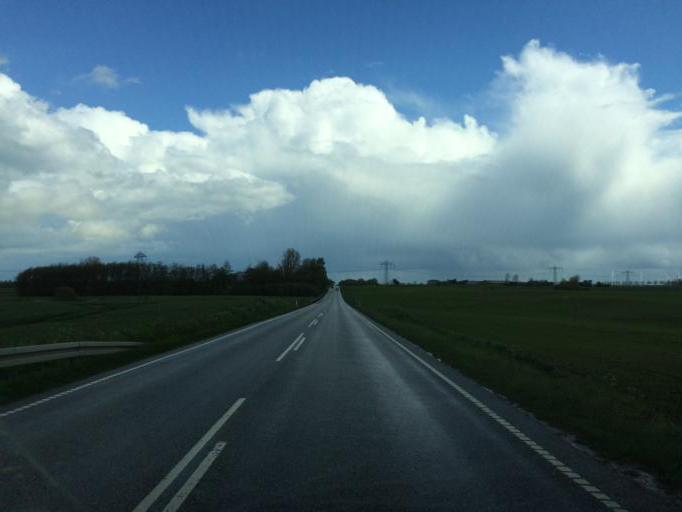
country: DK
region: Central Jutland
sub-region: Holstebro Kommune
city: Holstebro
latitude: 56.3939
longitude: 8.6651
